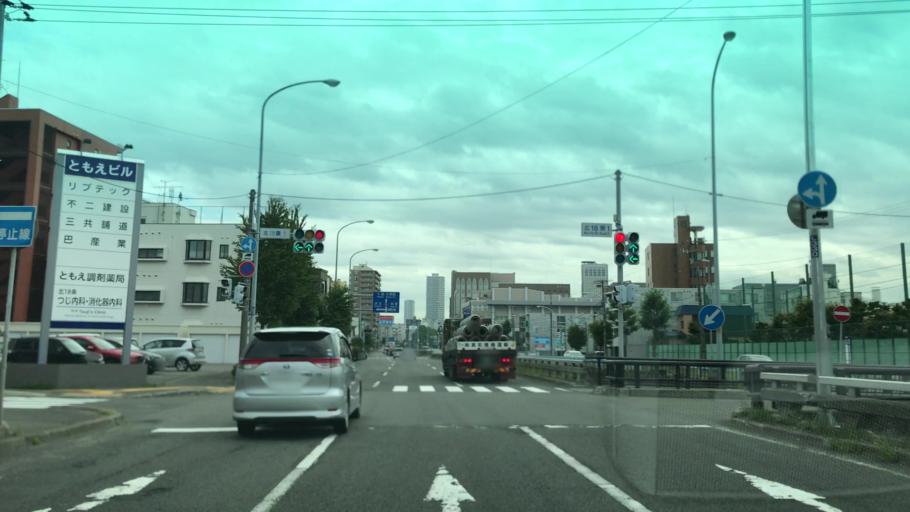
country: JP
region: Hokkaido
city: Sapporo
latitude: 43.0837
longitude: 141.3497
